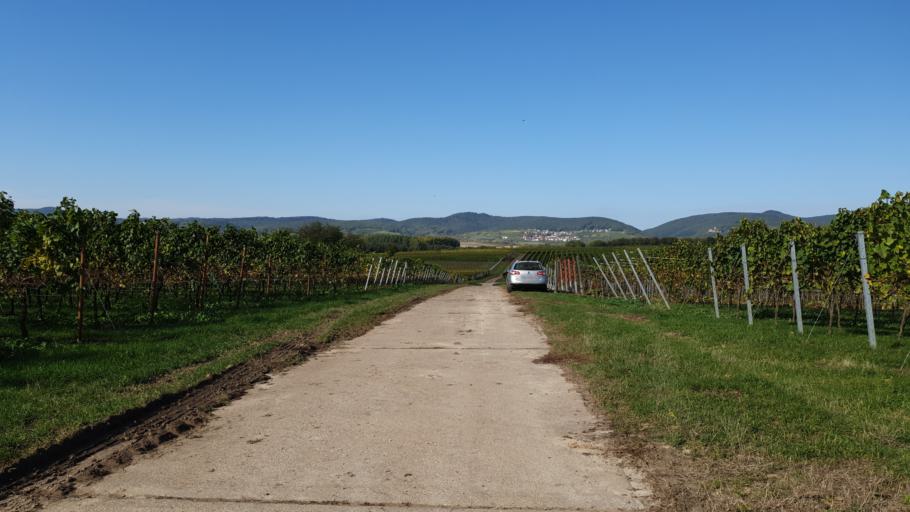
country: DE
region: Rheinland-Pfalz
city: Barbelroth
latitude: 49.1184
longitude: 8.0632
